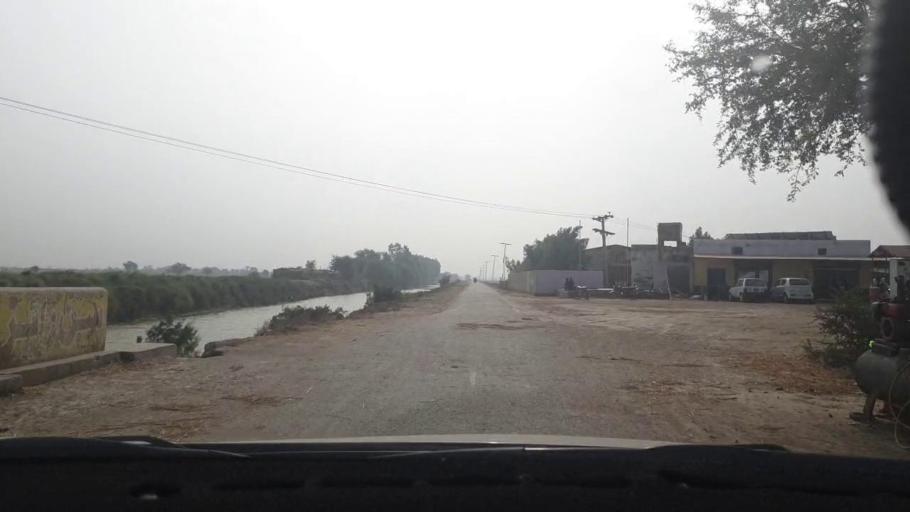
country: PK
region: Sindh
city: Tando Muhammad Khan
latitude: 25.0820
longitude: 68.5301
